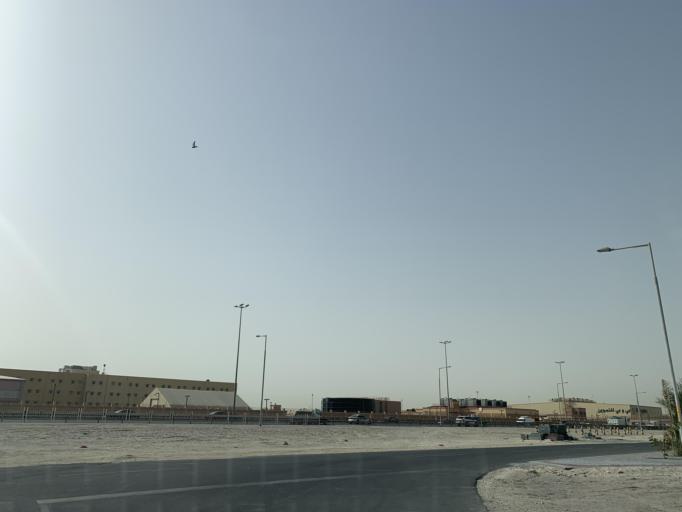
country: BH
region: Manama
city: Manama
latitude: 26.2105
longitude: 50.6168
